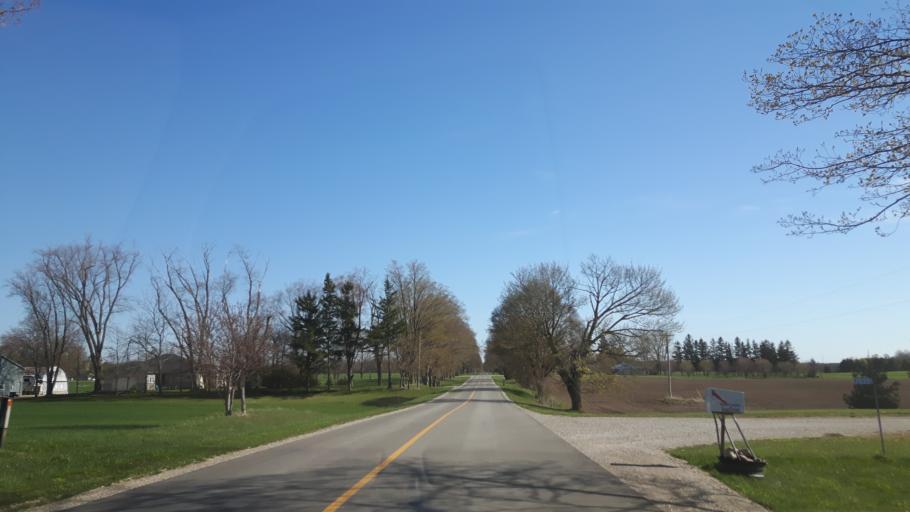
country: CA
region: Ontario
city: Goderich
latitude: 43.6267
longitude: -81.6644
